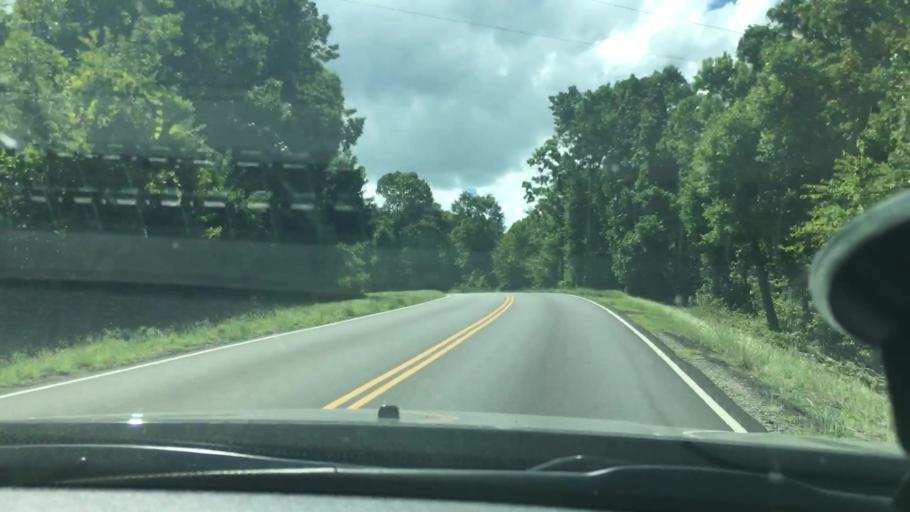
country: US
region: Oklahoma
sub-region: Sequoyah County
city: Vian
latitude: 35.6654
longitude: -94.9441
